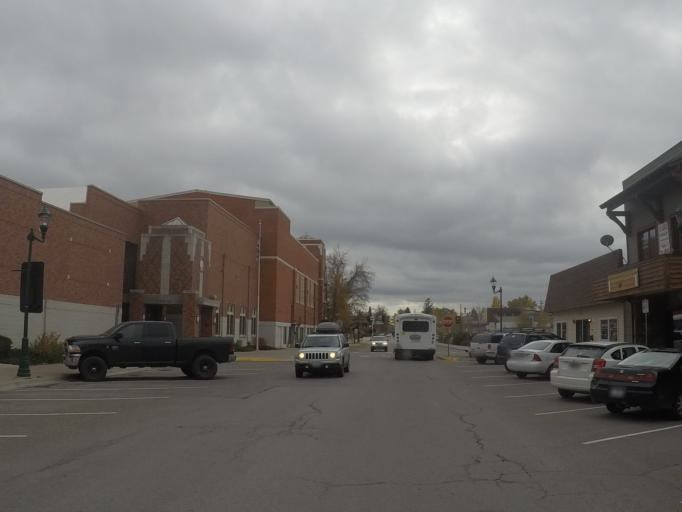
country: US
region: Montana
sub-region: Flathead County
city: Whitefish
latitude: 48.4121
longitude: -114.3353
